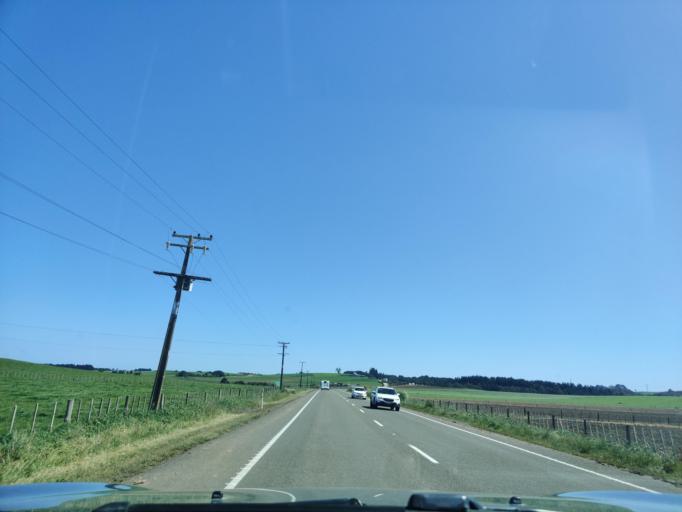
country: NZ
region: Manawatu-Wanganui
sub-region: Wanganui District
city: Wanganui
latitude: -39.8169
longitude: 174.8301
